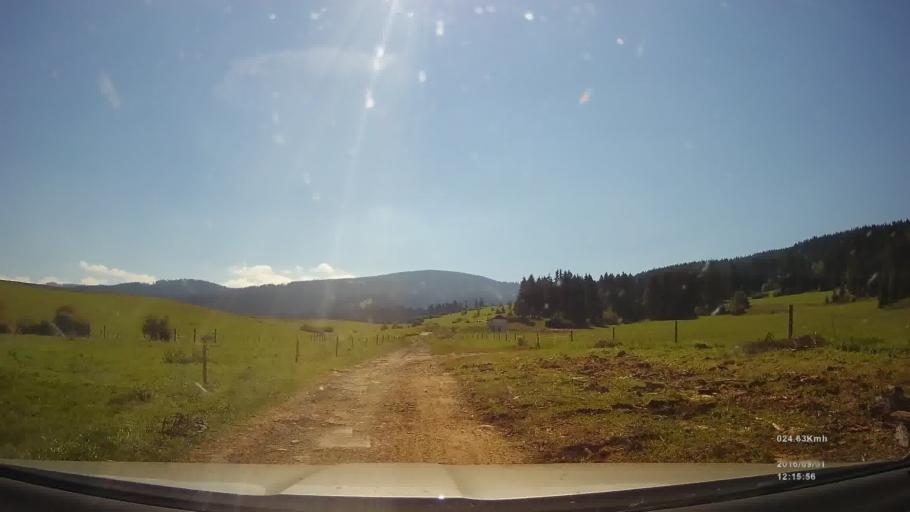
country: SK
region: Zilinsky
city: Ruzomberok
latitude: 49.0448
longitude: 19.4290
